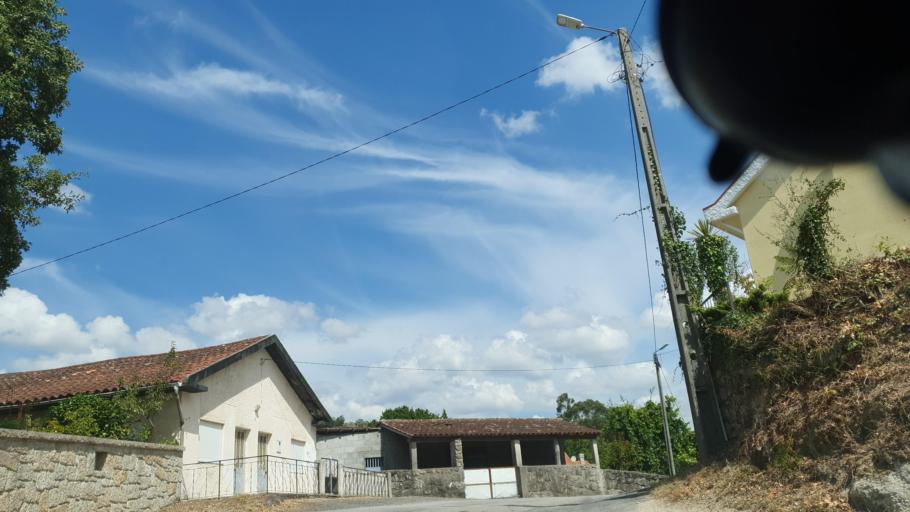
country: PT
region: Braga
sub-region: Vieira do Minho
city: Vieira do Minho
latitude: 41.7053
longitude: -8.0515
